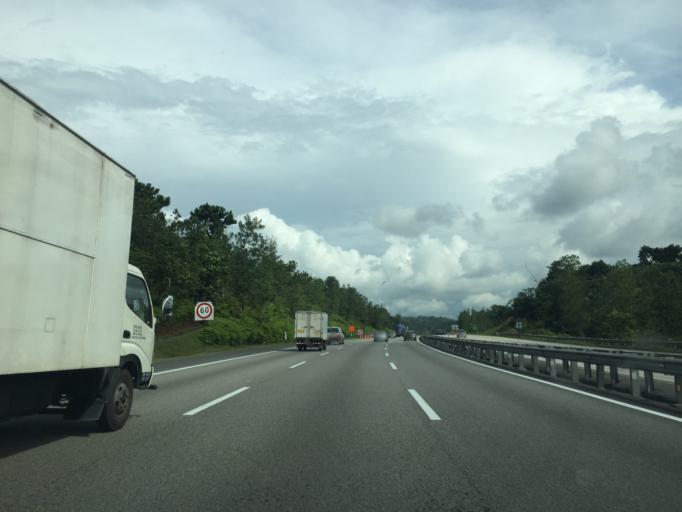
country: MY
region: Selangor
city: Batang Berjuntai
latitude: 3.5393
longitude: 101.5186
